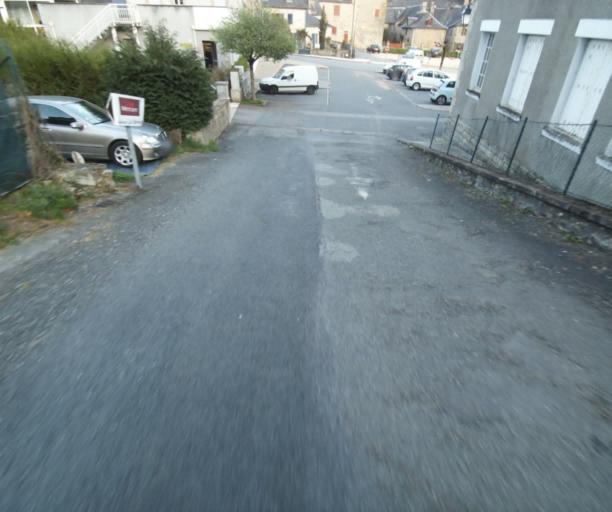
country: FR
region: Limousin
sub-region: Departement de la Correze
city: Correze
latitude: 45.3723
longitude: 1.8739
